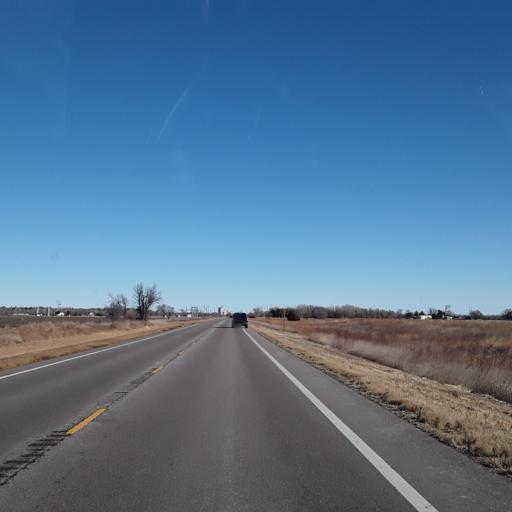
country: US
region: Kansas
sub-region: Pawnee County
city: Larned
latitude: 38.1540
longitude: -99.1302
